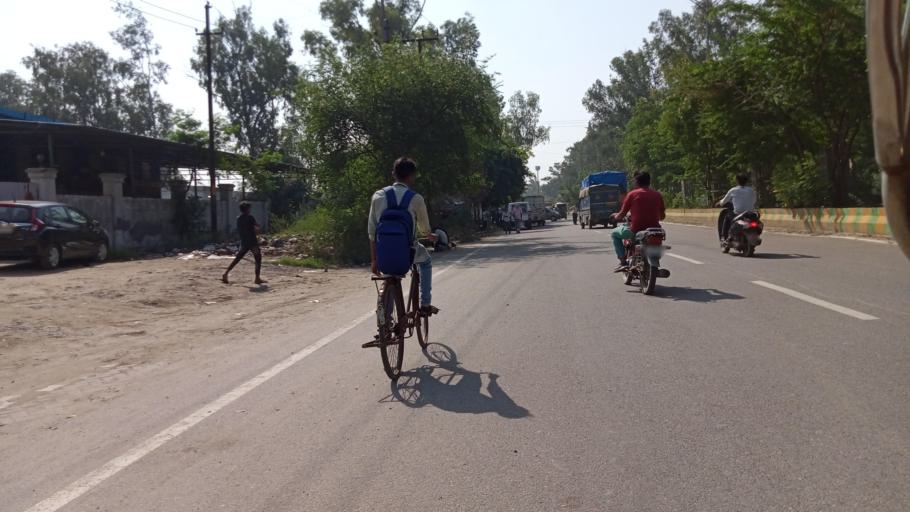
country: IN
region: Uttar Pradesh
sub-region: Ghaziabad
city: Ghaziabad
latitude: 28.6705
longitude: 77.3567
